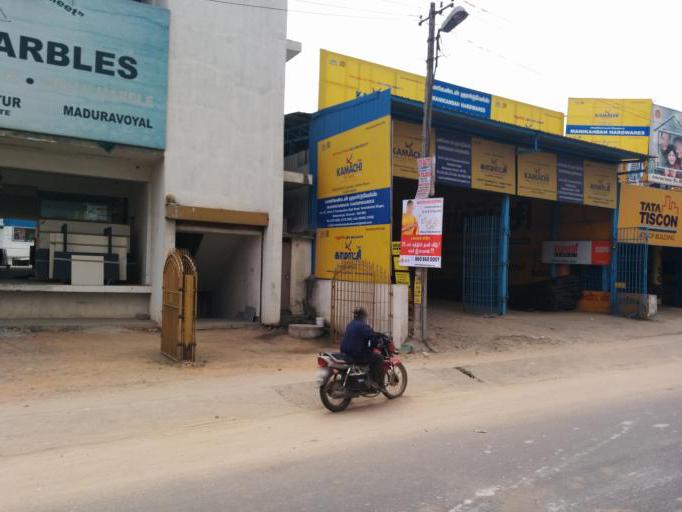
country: IN
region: Tamil Nadu
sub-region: Thiruvallur
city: Ambattur
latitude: 13.0680
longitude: 80.1791
